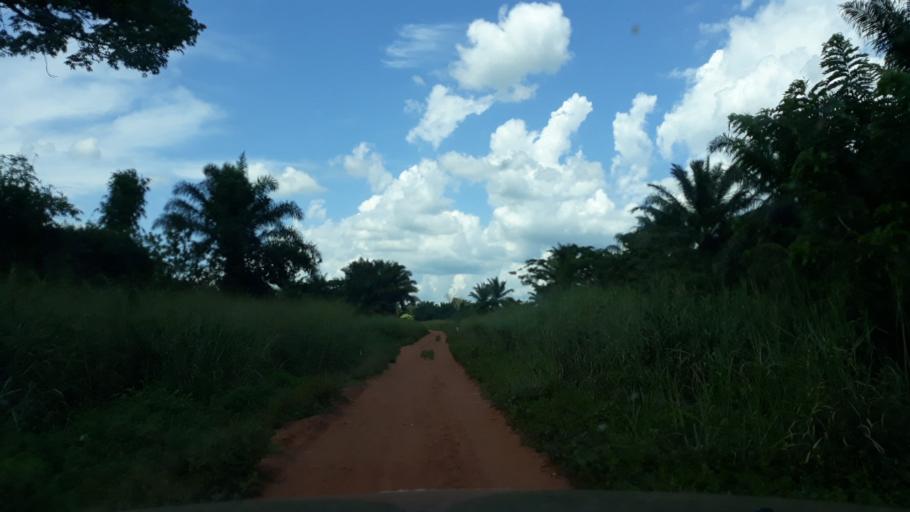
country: CD
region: Equateur
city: Businga
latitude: 3.4040
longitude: 20.3846
